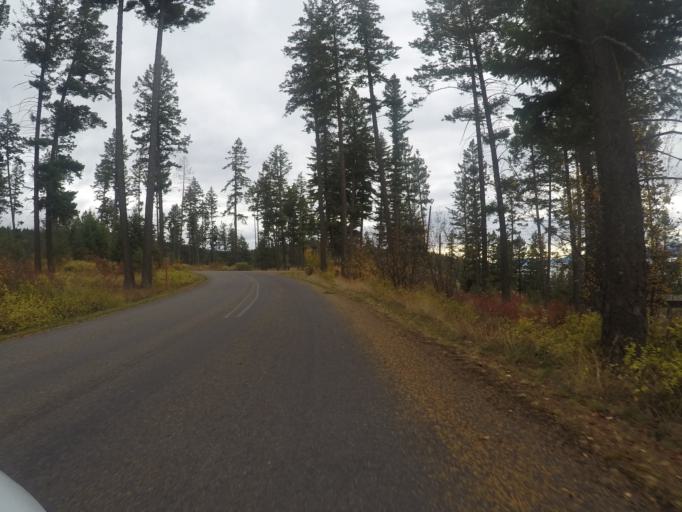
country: US
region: Montana
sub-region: Flathead County
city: Bigfork
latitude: 48.0528
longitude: -114.0787
